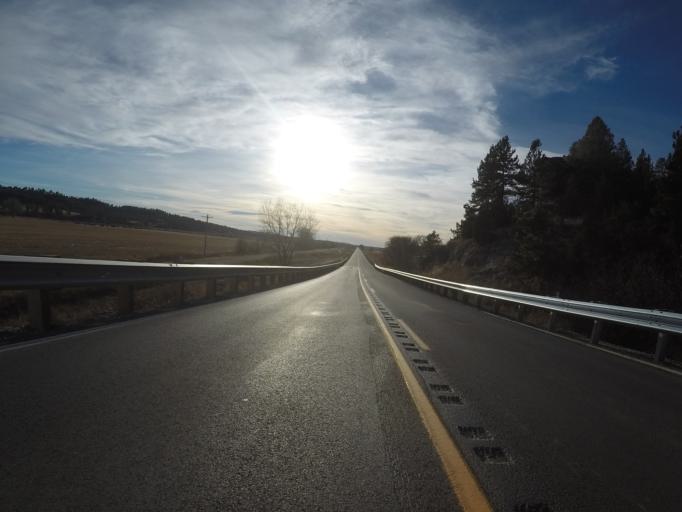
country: US
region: Montana
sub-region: Musselshell County
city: Roundup
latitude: 46.3973
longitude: -108.6065
